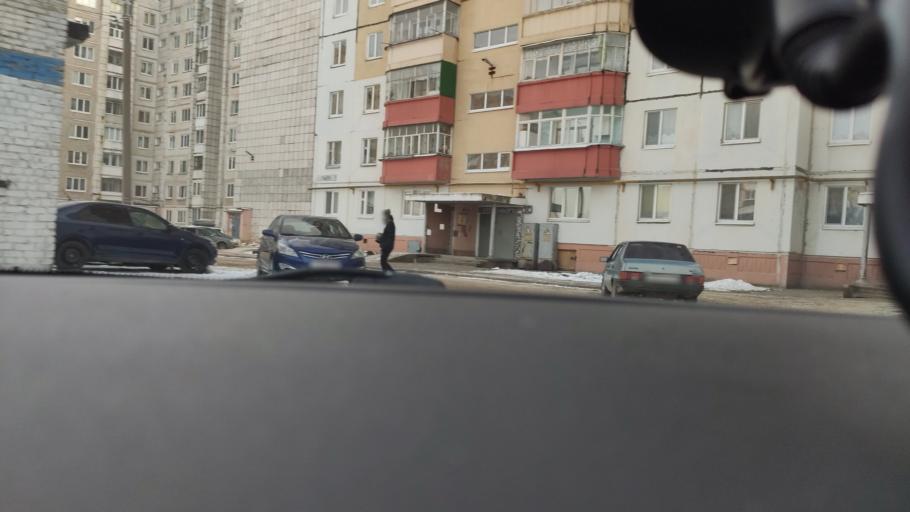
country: RU
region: Perm
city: Perm
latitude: 58.1101
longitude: 56.2878
